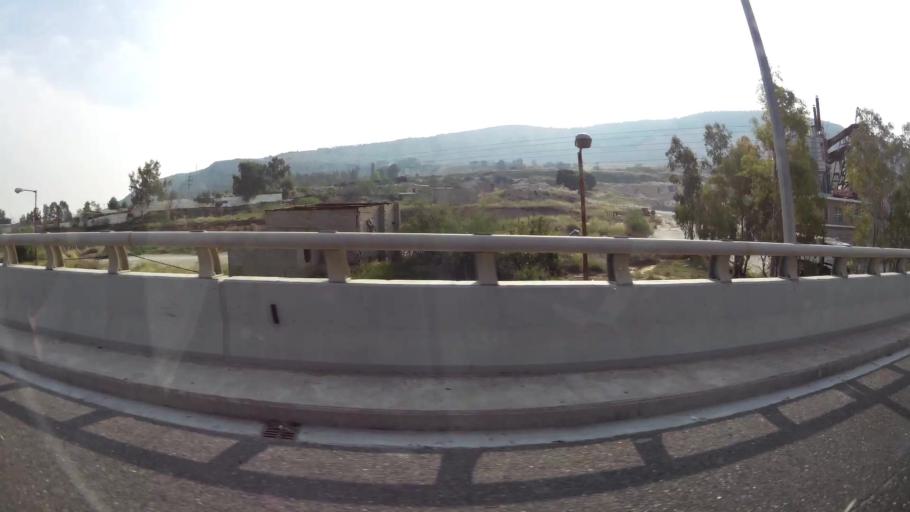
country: GR
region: Attica
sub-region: Nomarchia Athinas
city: Petroupolis
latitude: 38.0645
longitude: 23.6683
